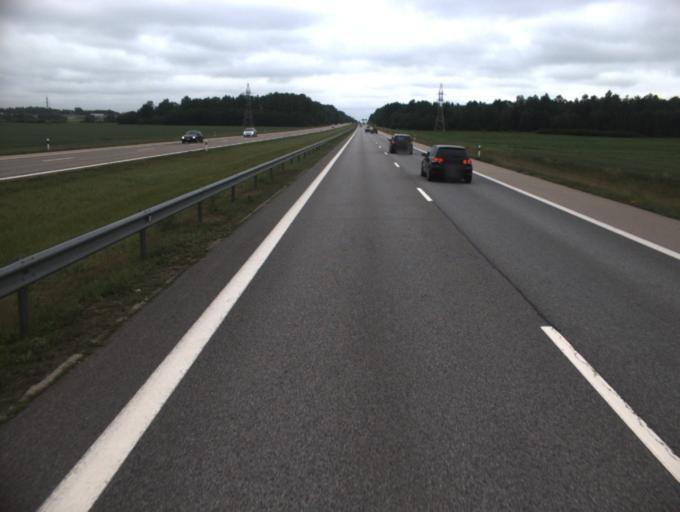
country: LT
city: Raseiniai
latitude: 55.3311
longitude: 23.1276
